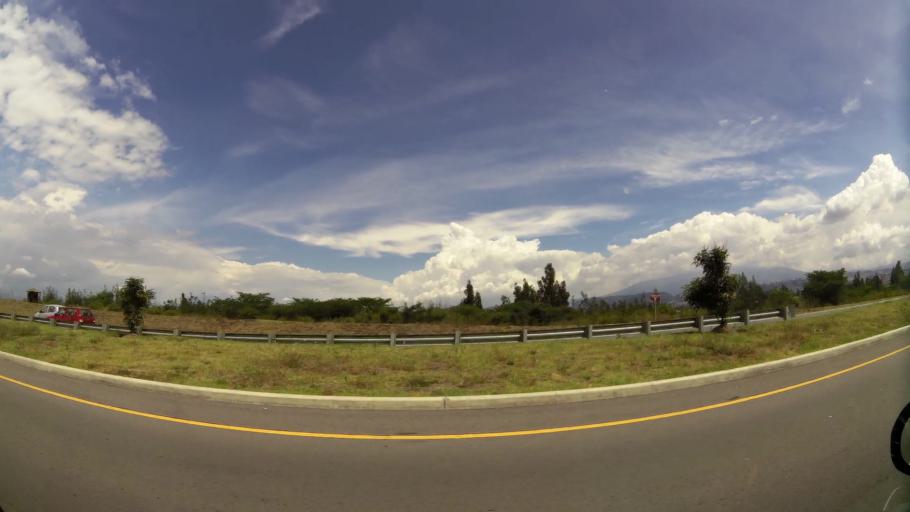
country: EC
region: Pichincha
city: Quito
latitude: -0.1483
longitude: -78.3537
